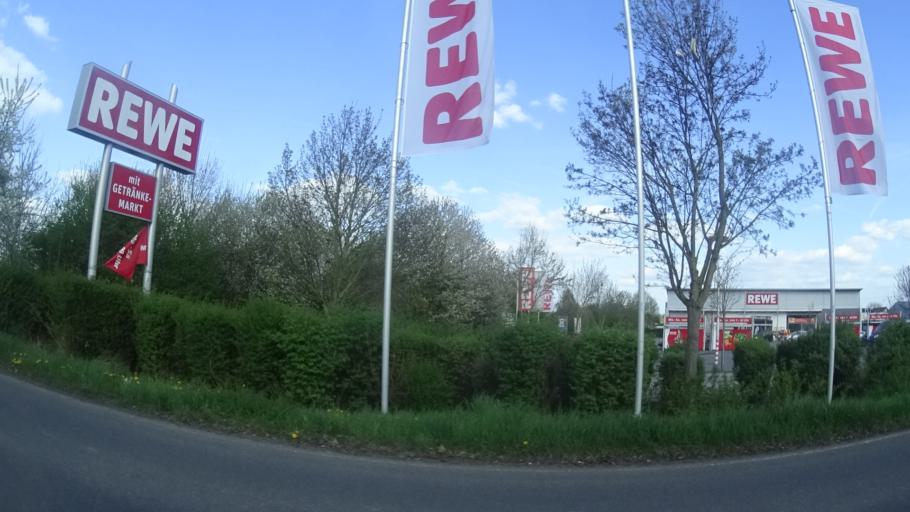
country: DE
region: Rheinland-Pfalz
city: Guntersblum
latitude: 49.8020
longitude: 8.3432
